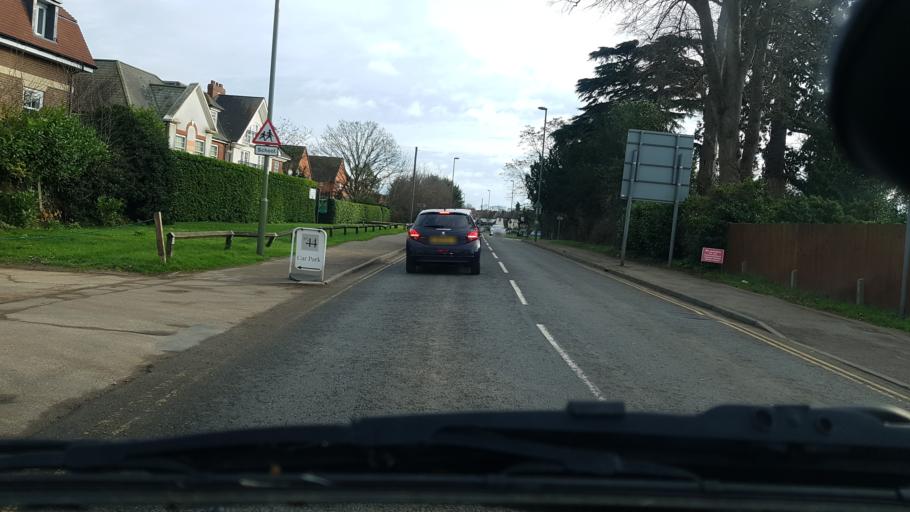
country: GB
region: England
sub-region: Surrey
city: Cobham
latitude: 51.3315
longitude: -0.4175
